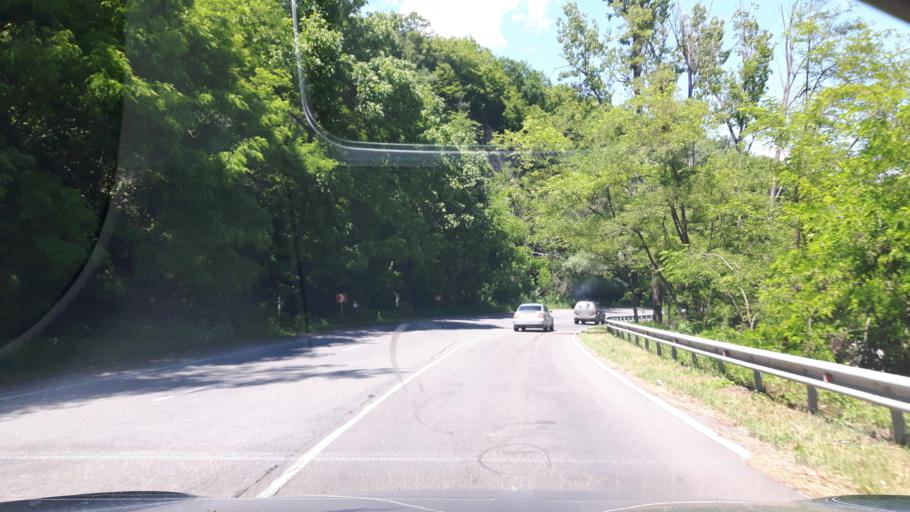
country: GE
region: Kakheti
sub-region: Gurjaani
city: Gurjaani
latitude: 41.6638
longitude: 45.8330
